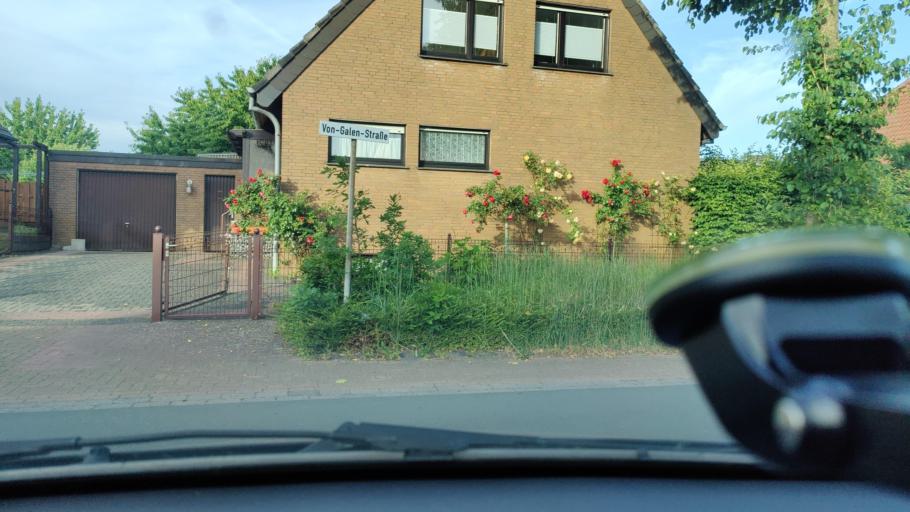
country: DE
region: North Rhine-Westphalia
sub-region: Regierungsbezirk Munster
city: Schoppingen
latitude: 52.0203
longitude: 7.2085
